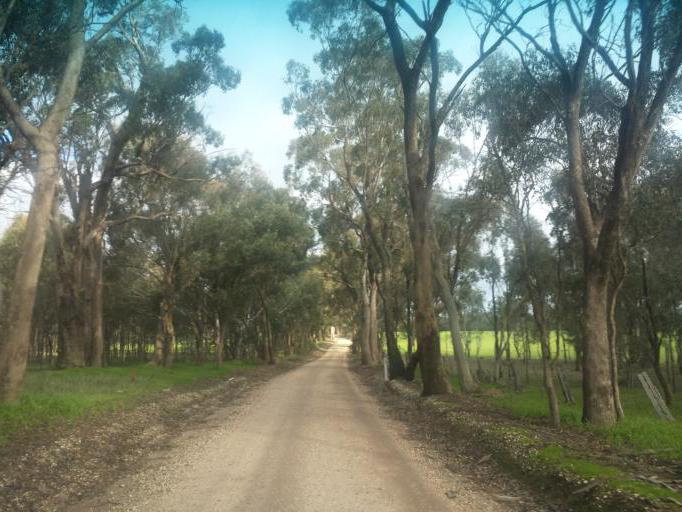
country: AU
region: Victoria
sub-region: Murrindindi
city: Kinglake West
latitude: -37.0415
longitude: 145.2318
